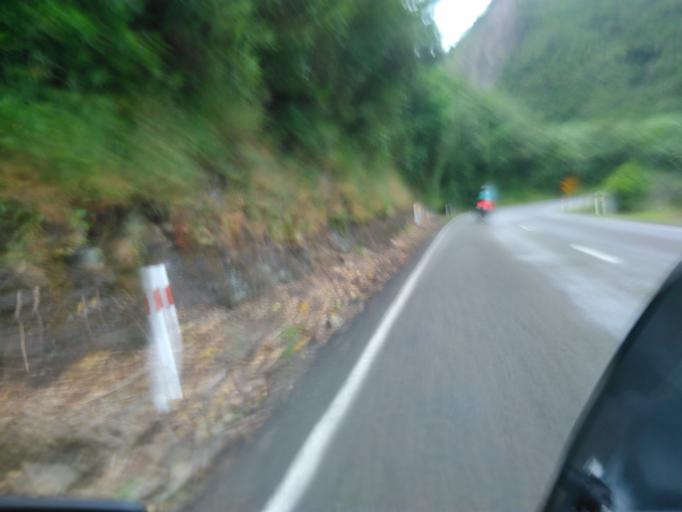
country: NZ
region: Bay of Plenty
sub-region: Opotiki District
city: Opotiki
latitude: -38.3000
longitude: 177.3933
